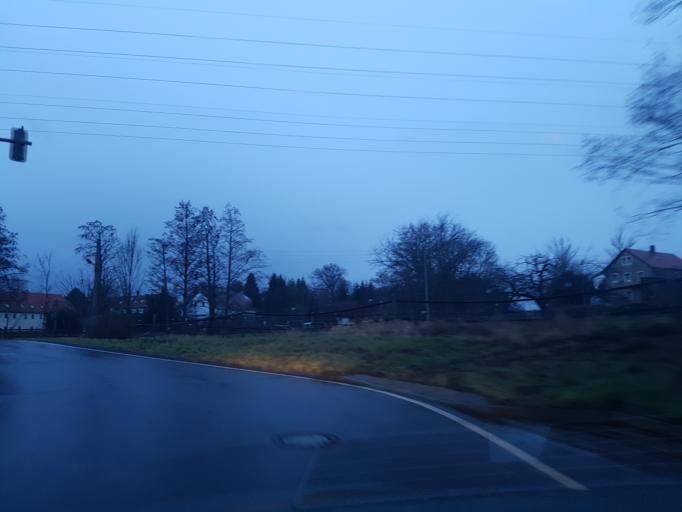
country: DE
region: Saxony
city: Priestewitz
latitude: 51.2453
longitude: 13.5201
